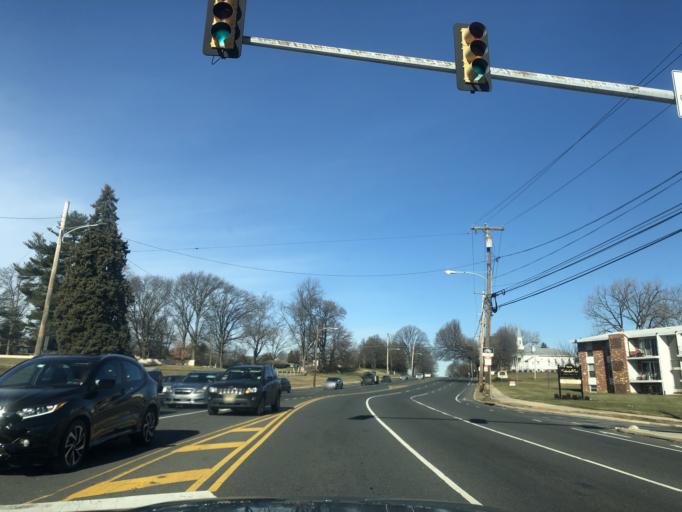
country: US
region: Pennsylvania
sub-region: Montgomery County
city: Flourtown
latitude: 40.0642
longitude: -75.2396
